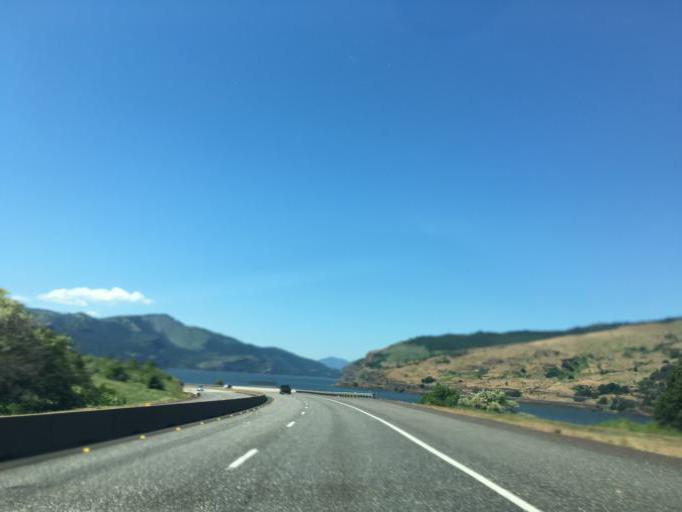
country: US
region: Washington
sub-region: Klickitat County
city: White Salmon
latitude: 45.6956
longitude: -121.3754
